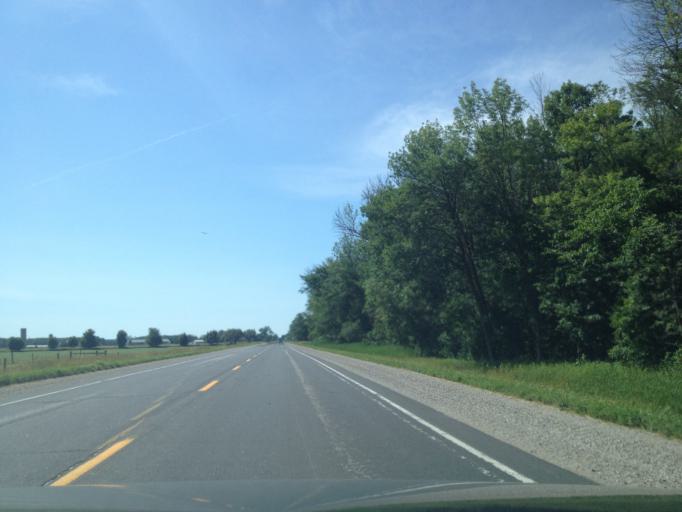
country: CA
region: Ontario
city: Stratford
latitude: 43.4948
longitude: -80.8610
